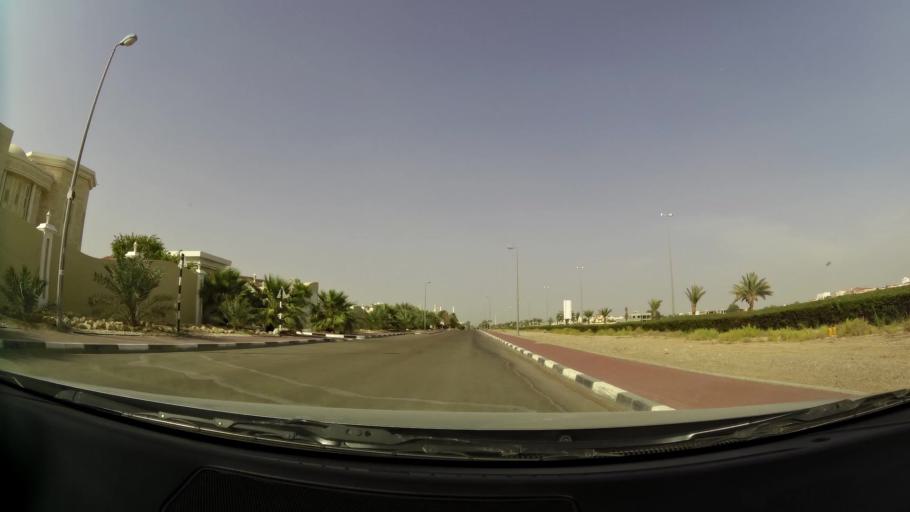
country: AE
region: Abu Dhabi
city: Al Ain
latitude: 24.2249
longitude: 55.6556
